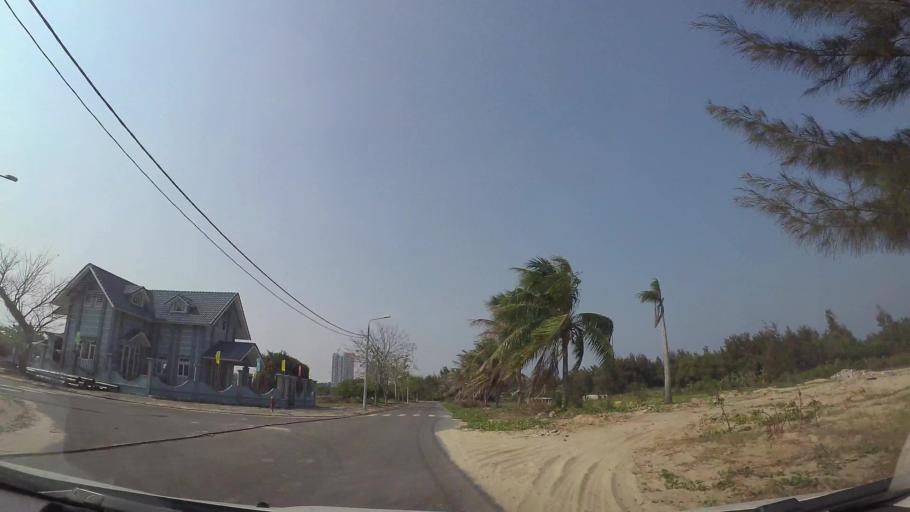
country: VN
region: Da Nang
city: Ngu Hanh Son
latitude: 15.9556
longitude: 108.2830
